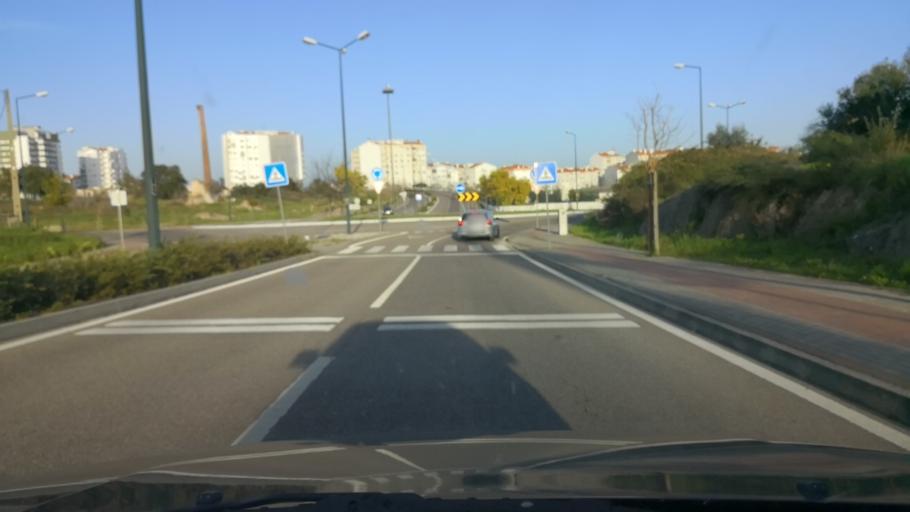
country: PT
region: Castelo Branco
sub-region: Castelo Branco
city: Castelo Branco
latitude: 39.8166
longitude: -7.4912
